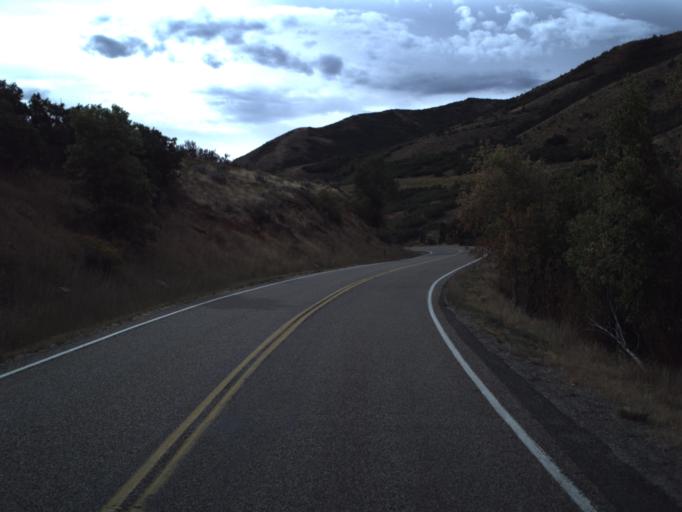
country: US
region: Utah
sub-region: Morgan County
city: Morgan
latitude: 40.9390
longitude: -111.6417
